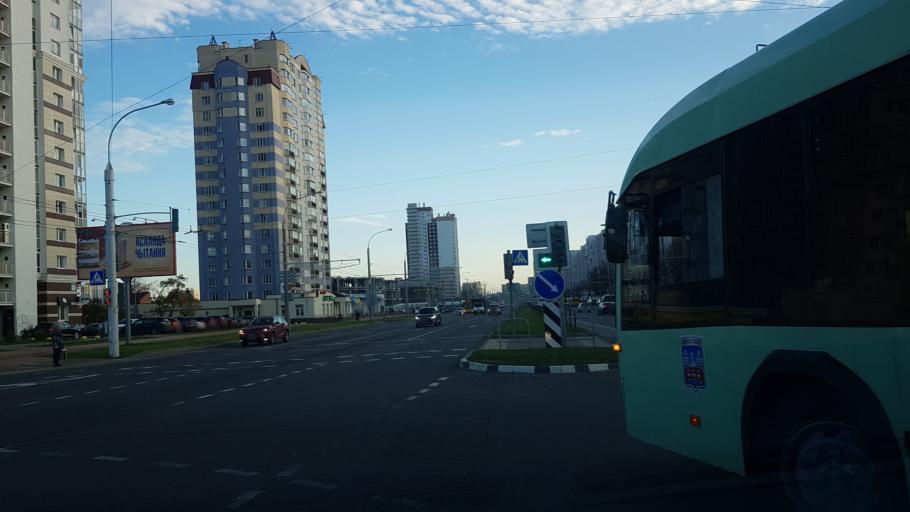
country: BY
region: Minsk
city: Minsk
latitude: 53.8836
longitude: 27.5678
